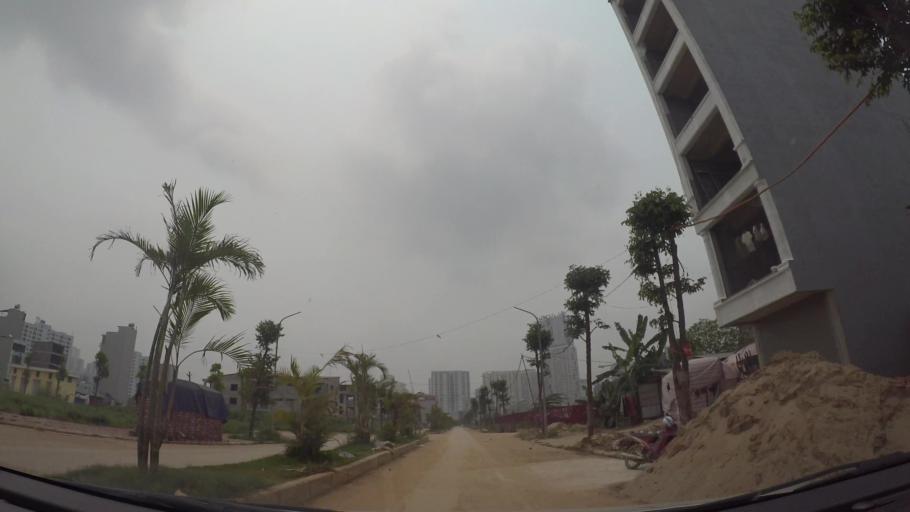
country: VN
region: Ha Noi
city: Ha Dong
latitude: 20.9787
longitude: 105.7688
